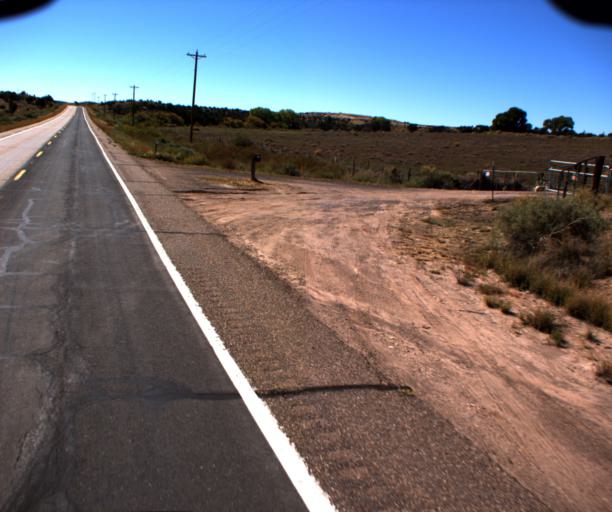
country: US
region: Arizona
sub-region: Apache County
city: Saint Johns
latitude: 34.4088
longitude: -109.4108
